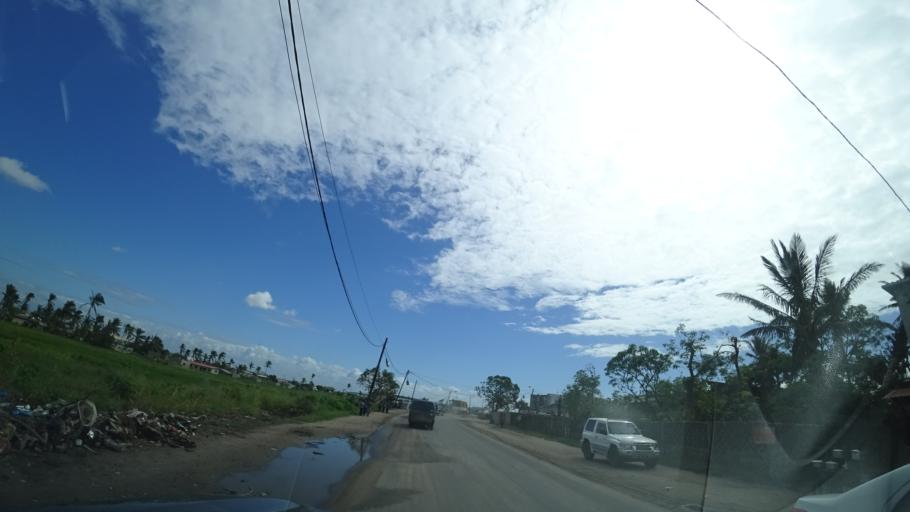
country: MZ
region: Sofala
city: Beira
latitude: -19.7804
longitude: 34.8735
